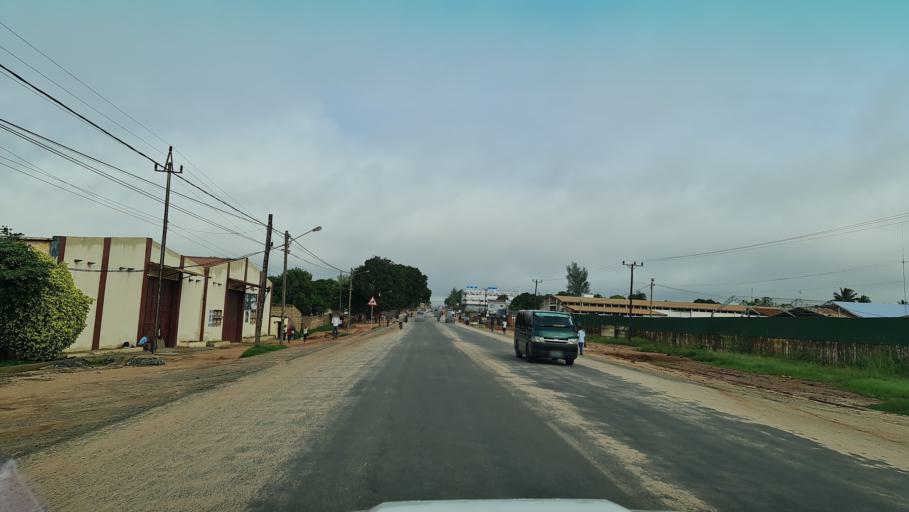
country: MZ
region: Nampula
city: Nampula
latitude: -15.1393
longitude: 39.2882
